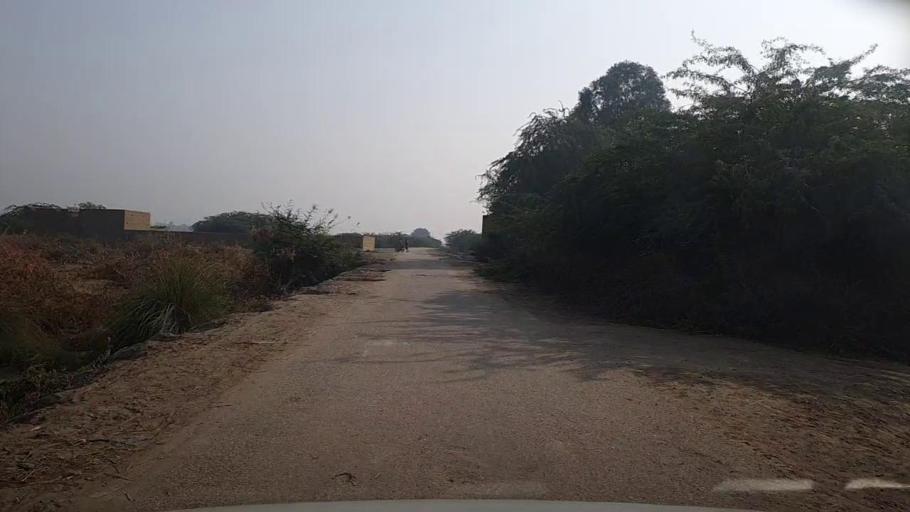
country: PK
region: Sindh
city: Kandiari
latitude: 27.0545
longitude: 68.4616
